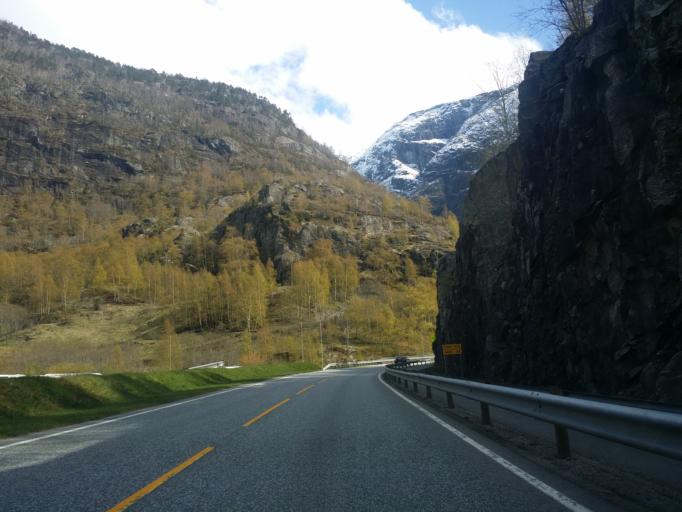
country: NO
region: Hordaland
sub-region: Eidfjord
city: Eidfjord
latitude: 60.4227
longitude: 7.1391
